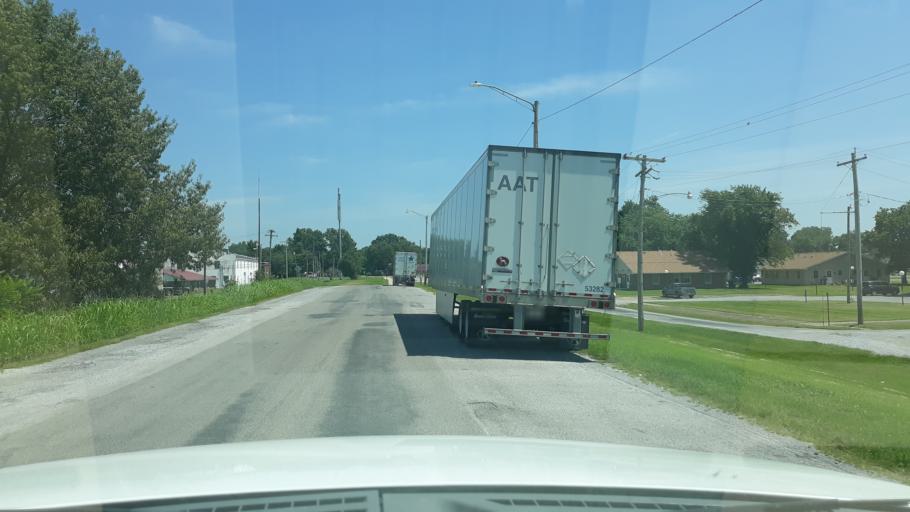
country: US
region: Illinois
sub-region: Saline County
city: Eldorado
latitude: 37.8113
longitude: -88.4399
